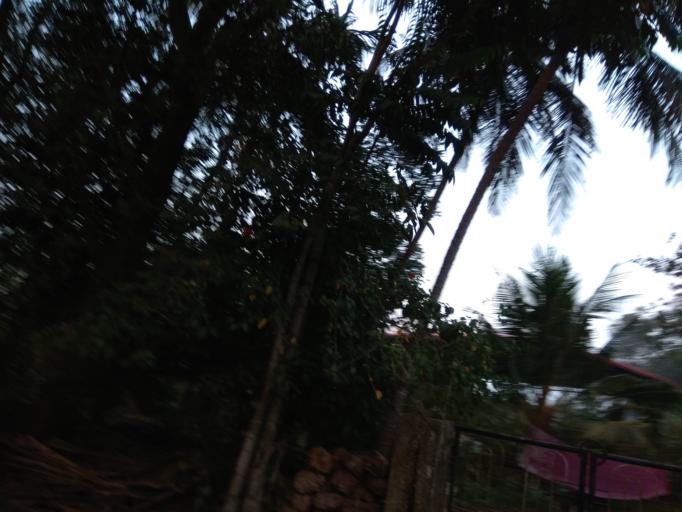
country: IN
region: Karnataka
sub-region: Dakshina Kannada
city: Mangalore
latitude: 12.9330
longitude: 74.8674
